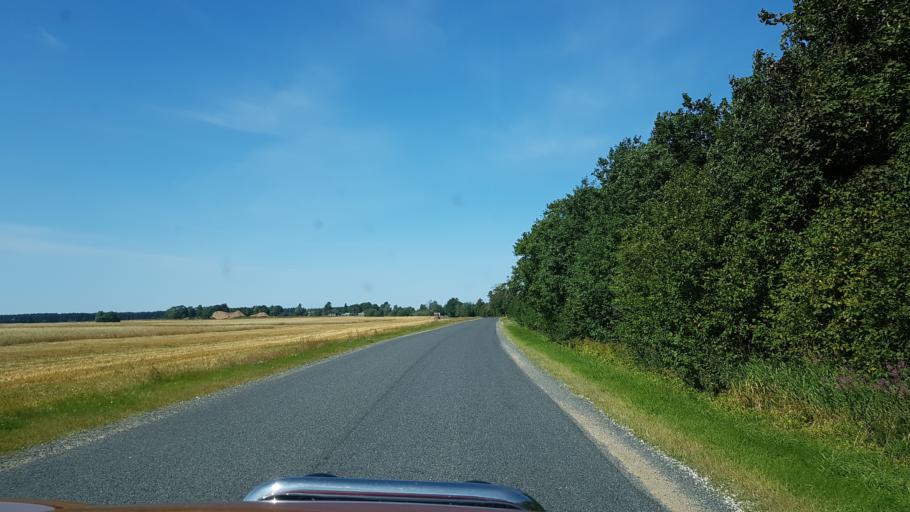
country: EE
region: Laeaene-Virumaa
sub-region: Rakke vald
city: Rakke
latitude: 59.0274
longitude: 26.3507
